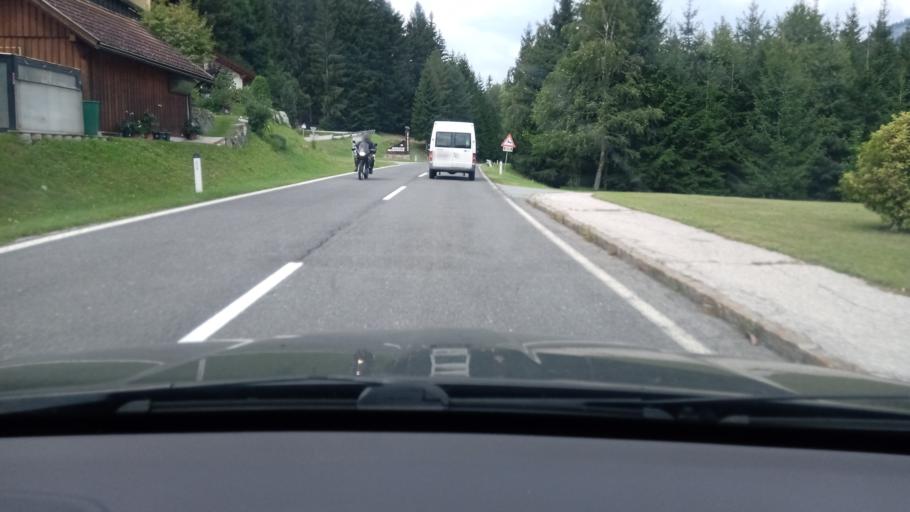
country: AT
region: Carinthia
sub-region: Politischer Bezirk Hermagor
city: Hermagor
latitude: 46.6459
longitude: 13.3354
